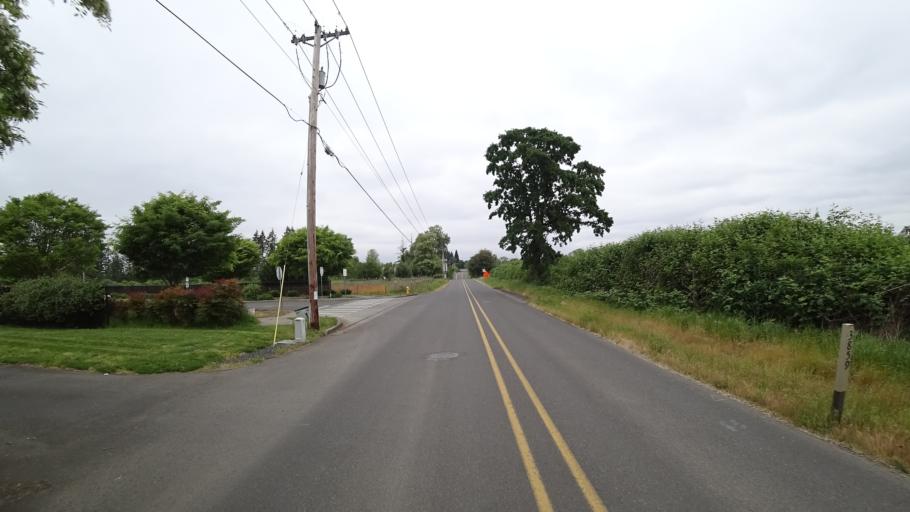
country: US
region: Oregon
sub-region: Washington County
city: Aloha
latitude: 45.4922
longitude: -122.9126
